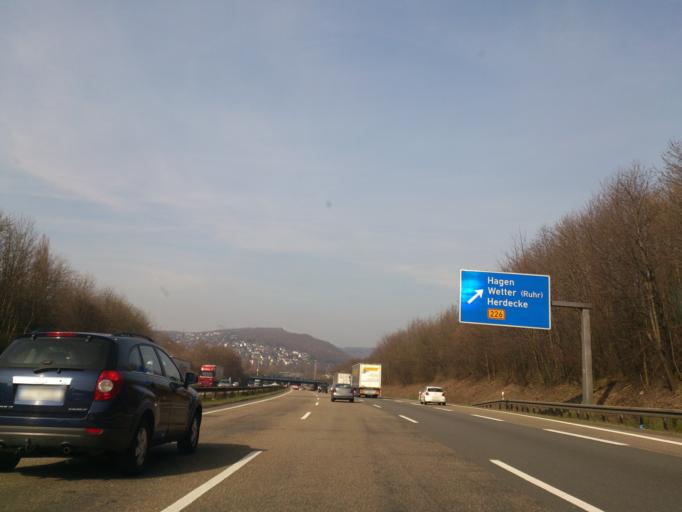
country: DE
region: North Rhine-Westphalia
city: Herdecke
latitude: 51.3818
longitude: 7.4364
